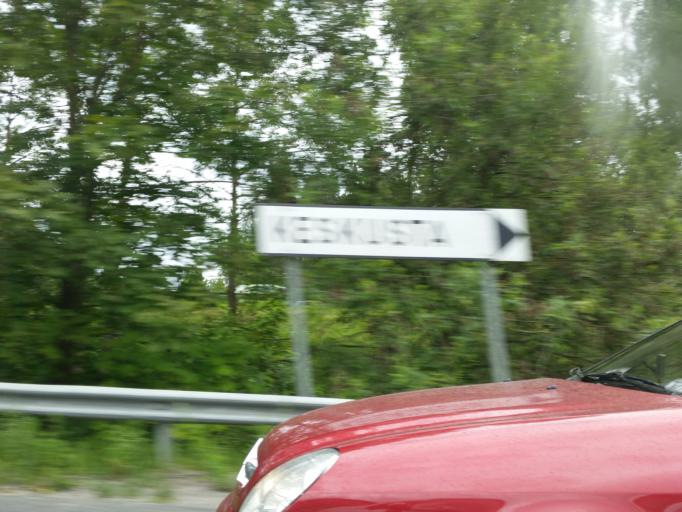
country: FI
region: Northern Savo
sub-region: Kuopio
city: Kuopio
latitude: 62.8964
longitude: 27.6508
